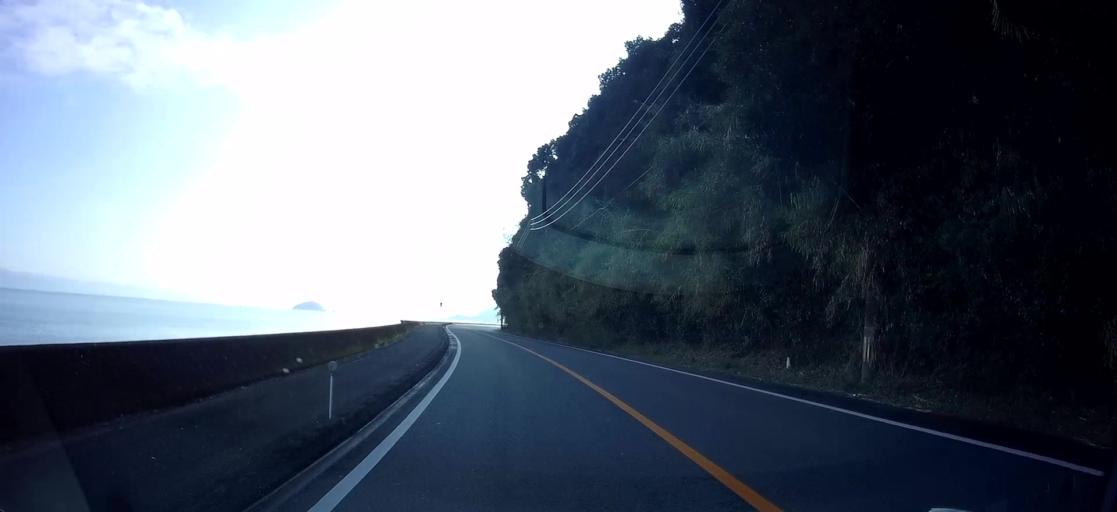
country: JP
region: Kumamoto
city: Yatsushiro
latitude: 32.4940
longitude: 130.4433
